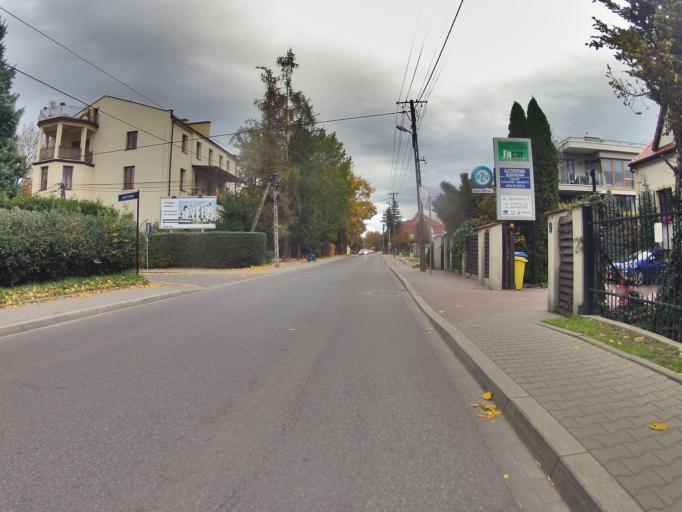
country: PL
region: Lesser Poland Voivodeship
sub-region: Powiat krakowski
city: Rzaska
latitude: 50.0679
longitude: 19.8749
